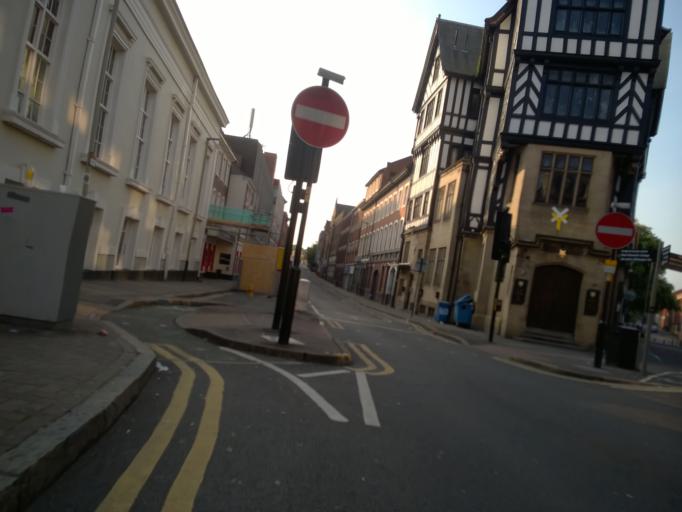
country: GB
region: England
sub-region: City of Leicester
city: Leicester
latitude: 52.6320
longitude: -1.1326
